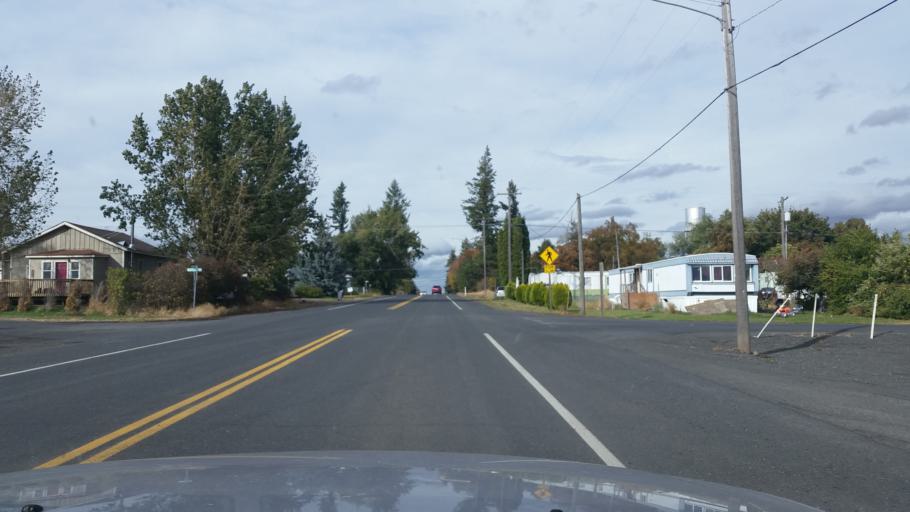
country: US
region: Washington
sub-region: Lincoln County
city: Davenport
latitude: 47.6473
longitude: -118.1577
